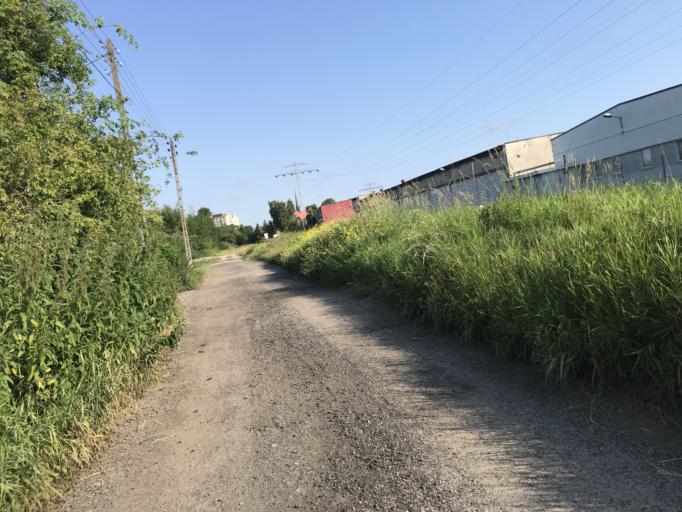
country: PL
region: Pomeranian Voivodeship
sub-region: Gdansk
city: Gdansk
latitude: 54.3466
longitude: 18.6788
